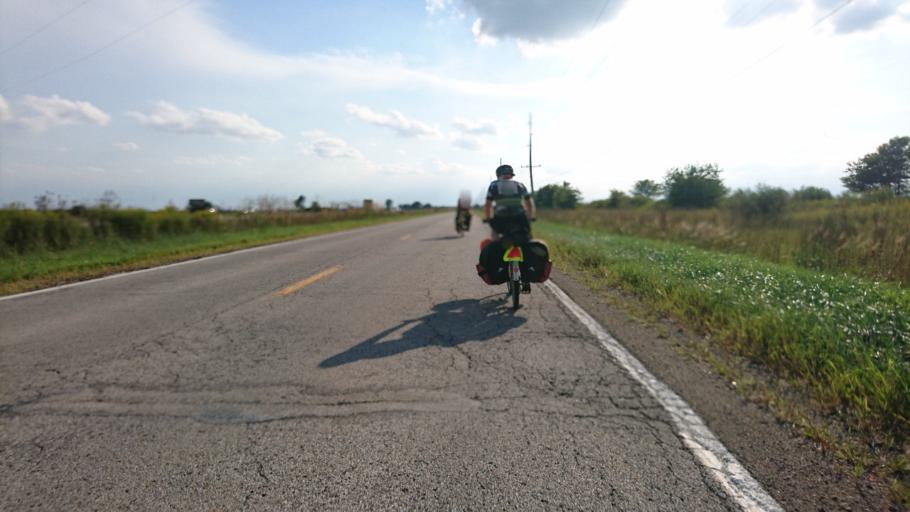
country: US
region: Illinois
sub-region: Logan County
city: Atlanta
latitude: 40.2991
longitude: -89.1874
